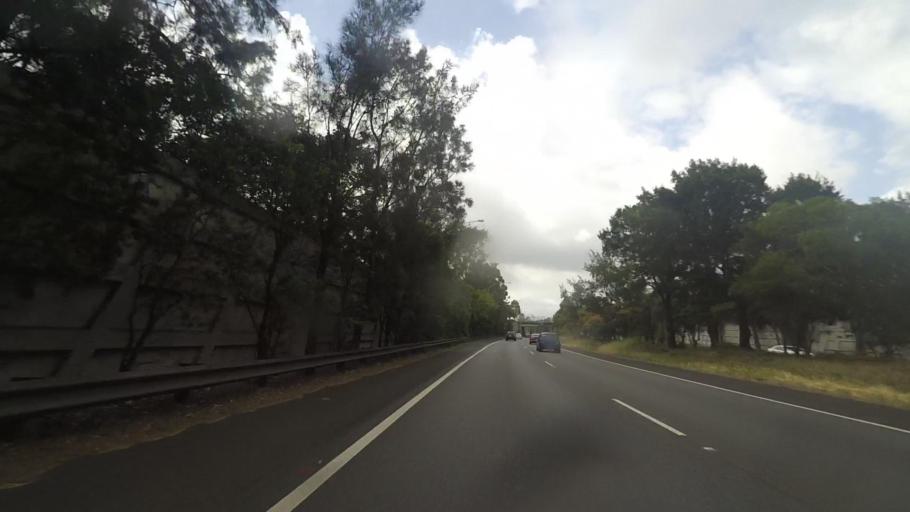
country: AU
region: New South Wales
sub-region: Wollongong
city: Mangerton
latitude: -34.4369
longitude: 150.8679
